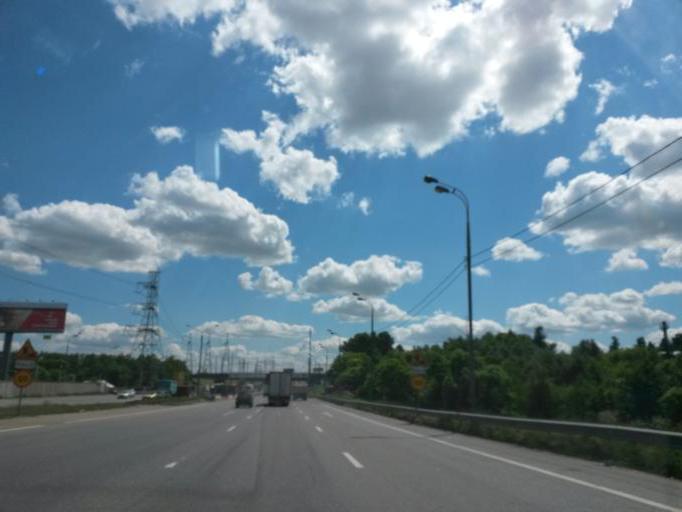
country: RU
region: Moscow
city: Annino
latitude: 55.5670
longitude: 37.6009
